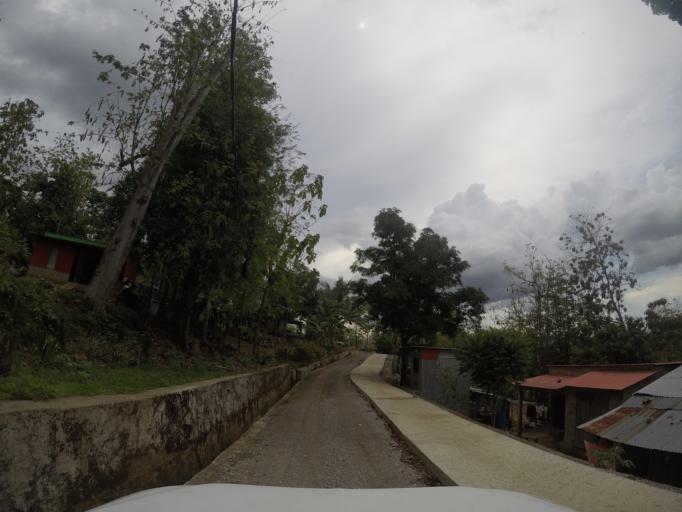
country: TL
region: Bobonaro
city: Maliana
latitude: -8.9965
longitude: 125.2130
